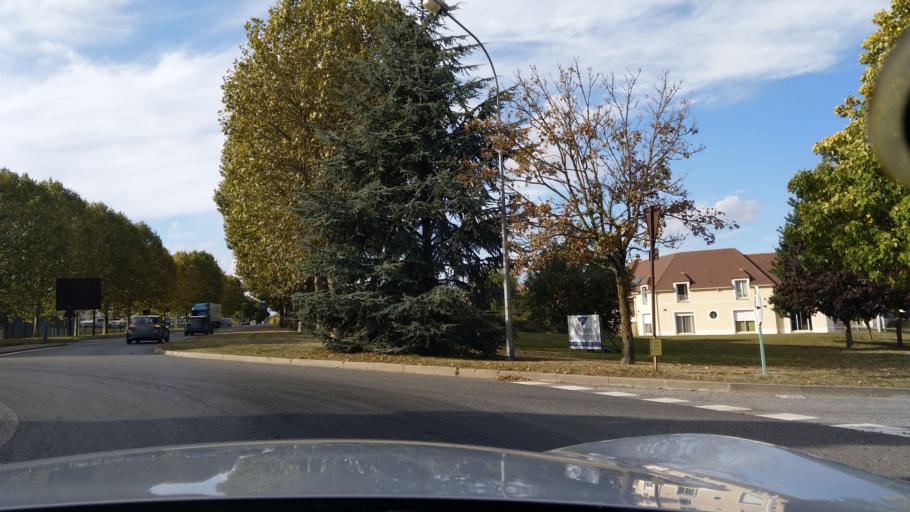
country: FR
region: Ile-de-France
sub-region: Departement de Seine-et-Marne
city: Saint-Soupplets
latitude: 49.0320
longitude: 2.8076
